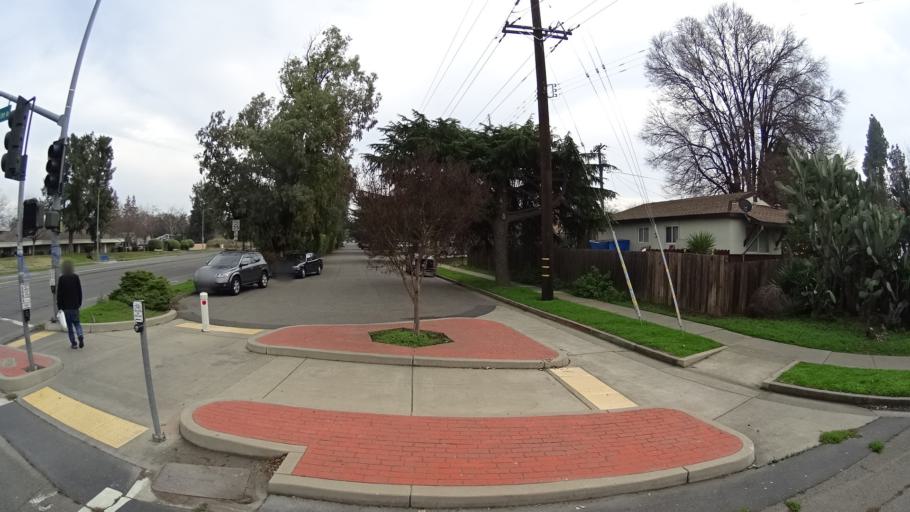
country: US
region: California
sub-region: Yolo County
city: Davis
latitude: 38.5623
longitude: -121.7310
